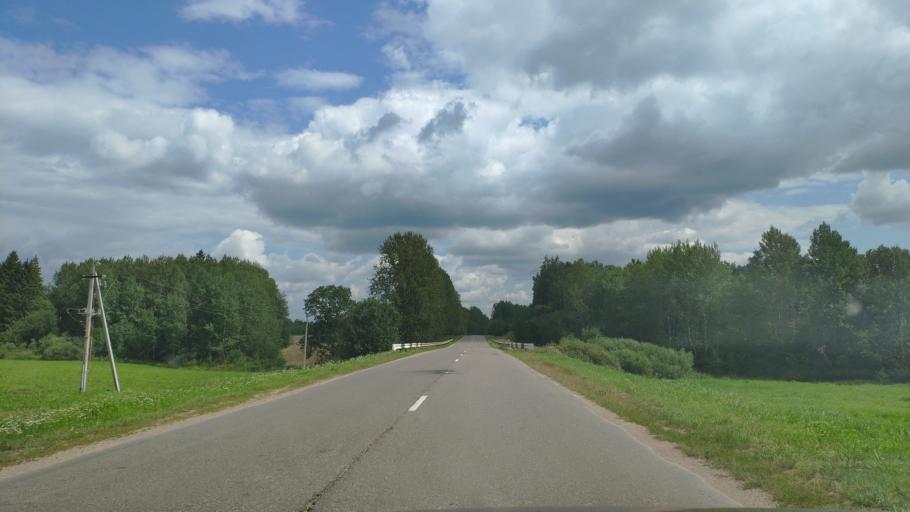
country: BY
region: Minsk
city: Khatsyezhyna
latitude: 53.8798
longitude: 27.2828
